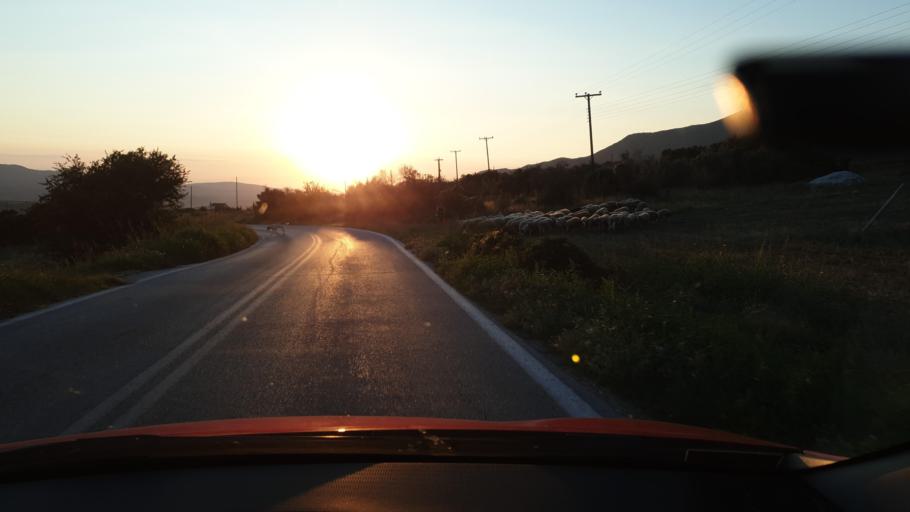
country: GR
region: Central Macedonia
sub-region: Nomos Chalkidikis
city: Galatista
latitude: 40.4681
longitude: 23.2646
